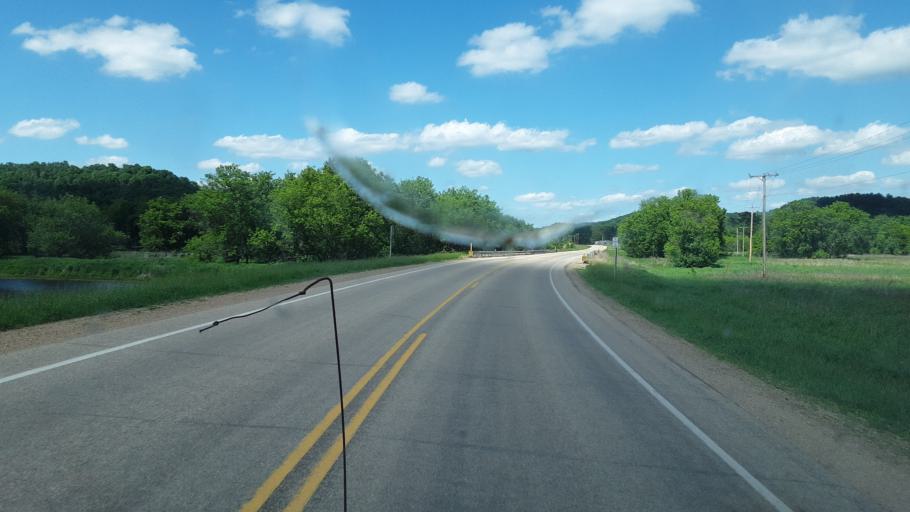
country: US
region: Wisconsin
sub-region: Richland County
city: Richland Center
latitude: 43.3462
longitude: -90.2813
